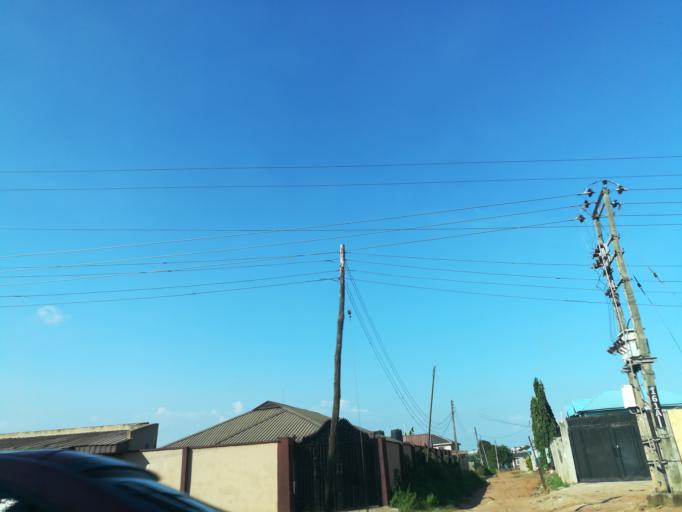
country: NG
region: Lagos
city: Ikorodu
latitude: 6.5721
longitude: 3.5300
